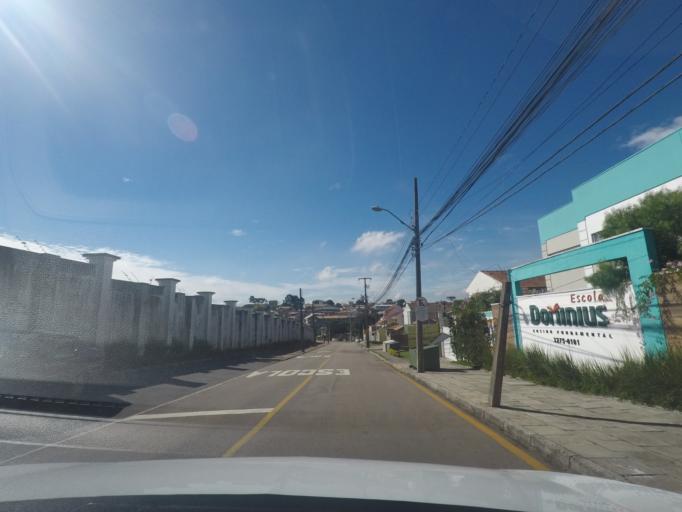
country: BR
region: Parana
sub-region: Sao Jose Dos Pinhais
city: Sao Jose dos Pinhais
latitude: -25.5037
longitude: -49.2697
